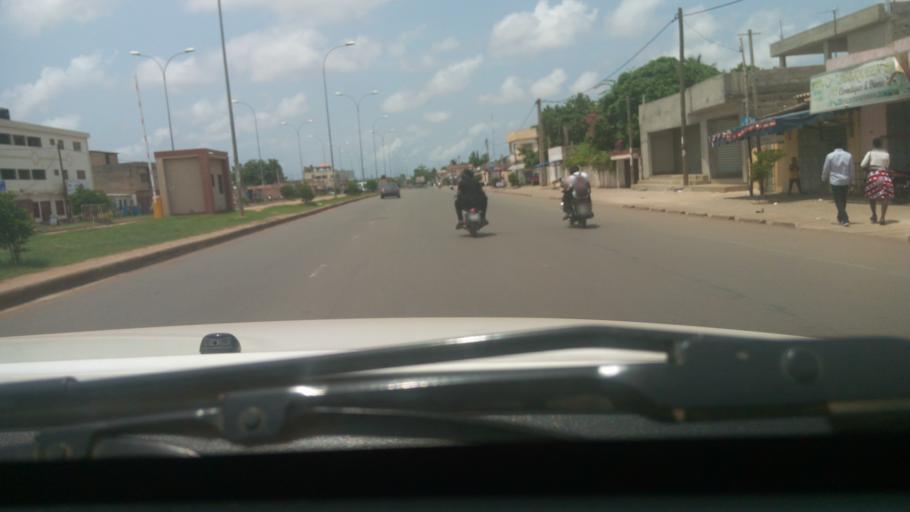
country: TG
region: Maritime
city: Lome
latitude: 6.1999
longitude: 1.1970
